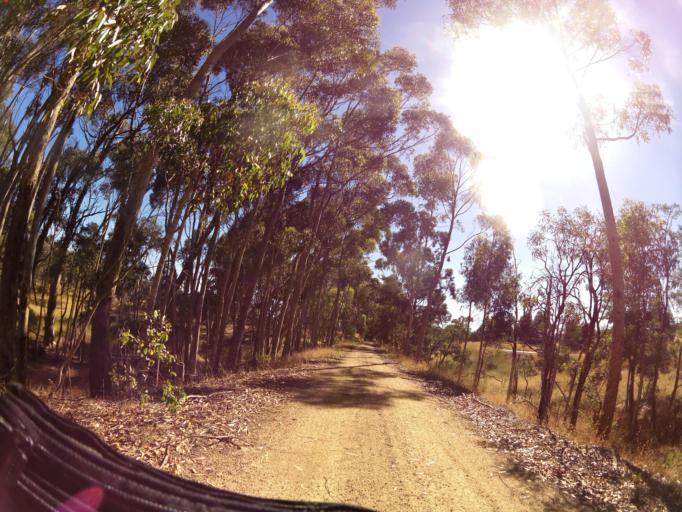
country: AU
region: Victoria
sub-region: Ballarat North
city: Delacombe
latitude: -37.6751
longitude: 143.4446
